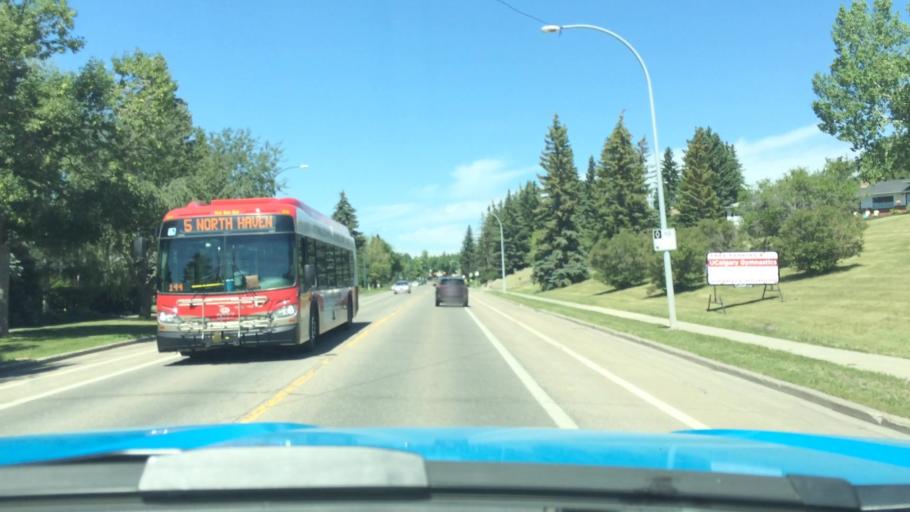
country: CA
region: Alberta
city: Calgary
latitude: 51.0798
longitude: -114.0875
